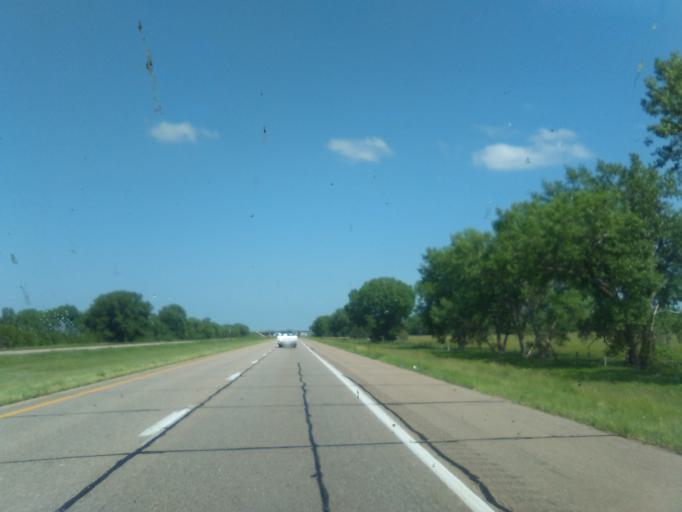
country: US
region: Nebraska
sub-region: Buffalo County
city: Kearney
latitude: 40.6821
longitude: -99.2979
